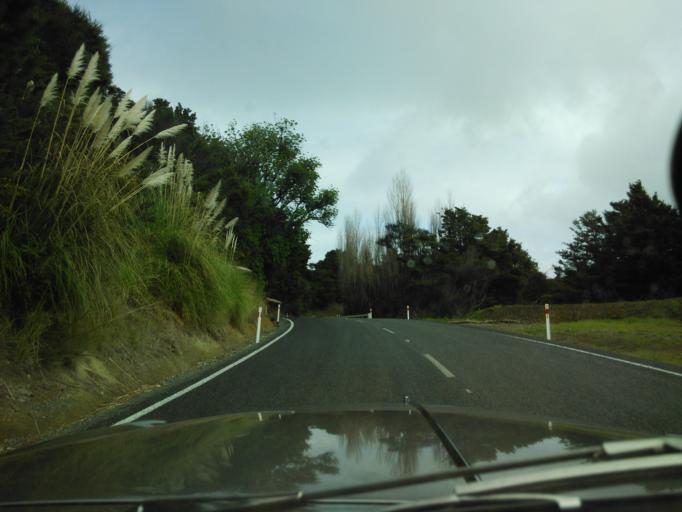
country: NZ
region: Auckland
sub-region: Auckland
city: Wellsford
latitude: -36.3460
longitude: 174.3652
